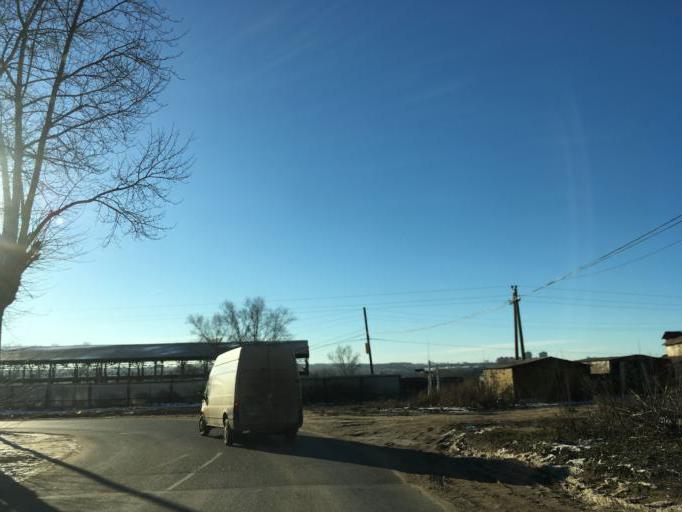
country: RU
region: Tula
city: Tula
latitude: 54.1851
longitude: 37.6921
